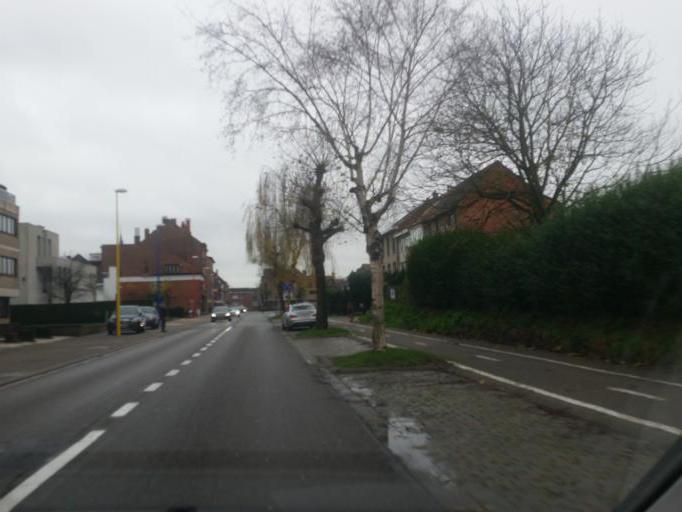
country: BE
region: Flanders
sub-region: Provincie Vlaams-Brabant
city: Grimbergen
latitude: 50.9139
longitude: 4.3581
